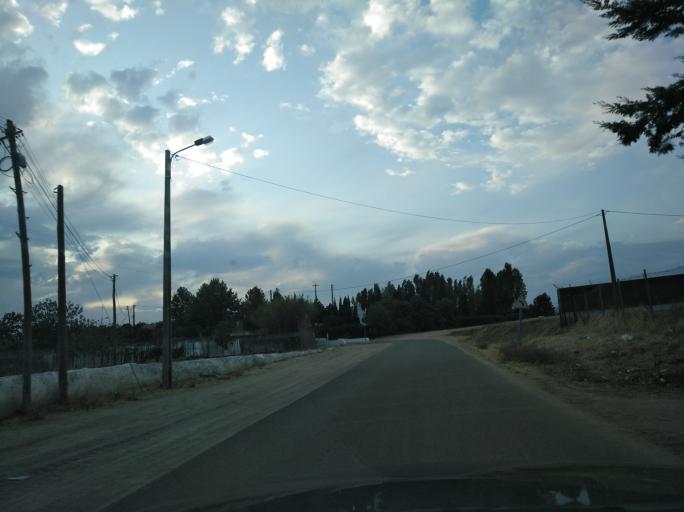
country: PT
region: Portalegre
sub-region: Campo Maior
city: Campo Maior
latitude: 39.0184
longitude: -7.0567
